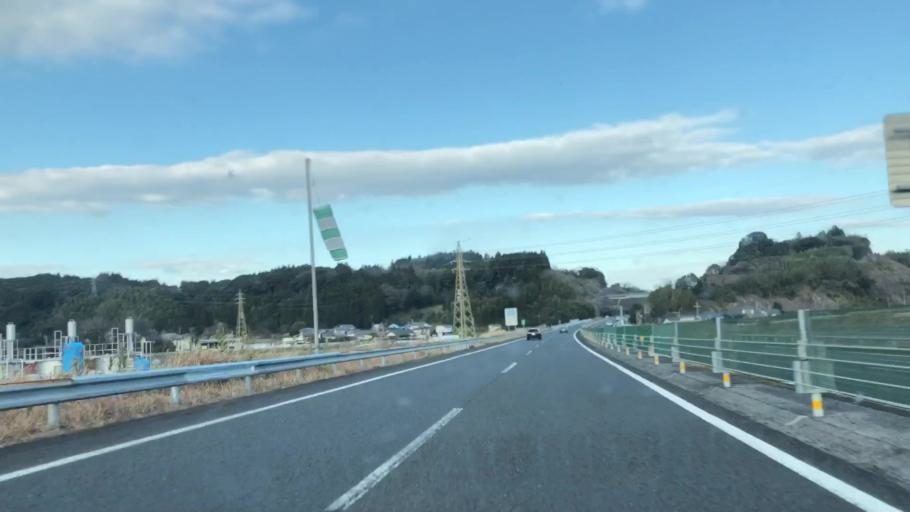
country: JP
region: Miyazaki
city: Miyazaki-shi
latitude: 31.8610
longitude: 131.3796
